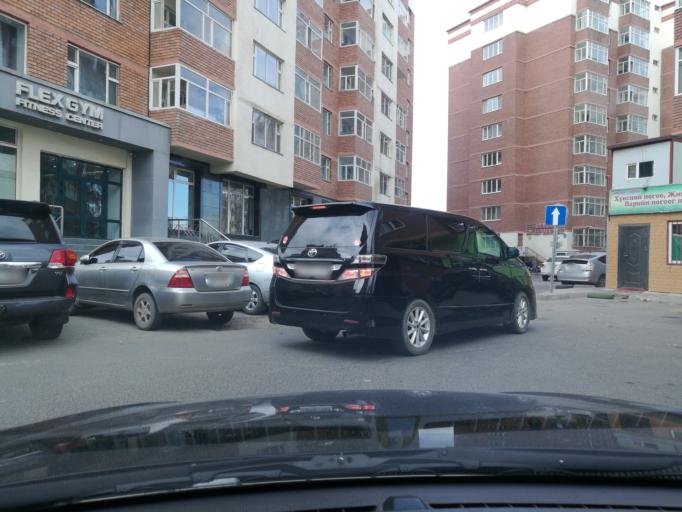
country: MN
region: Ulaanbaatar
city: Ulaanbaatar
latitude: 47.9015
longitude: 106.9194
